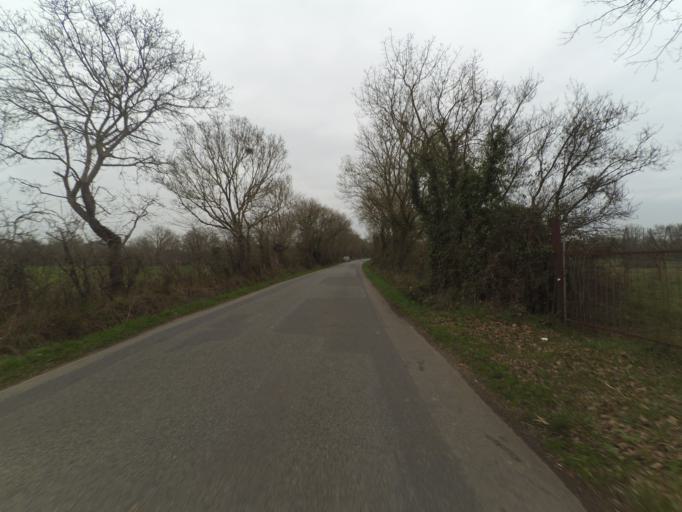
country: FR
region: Pays de la Loire
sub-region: Departement de la Loire-Atlantique
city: Indre
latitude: 47.2282
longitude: -1.6848
